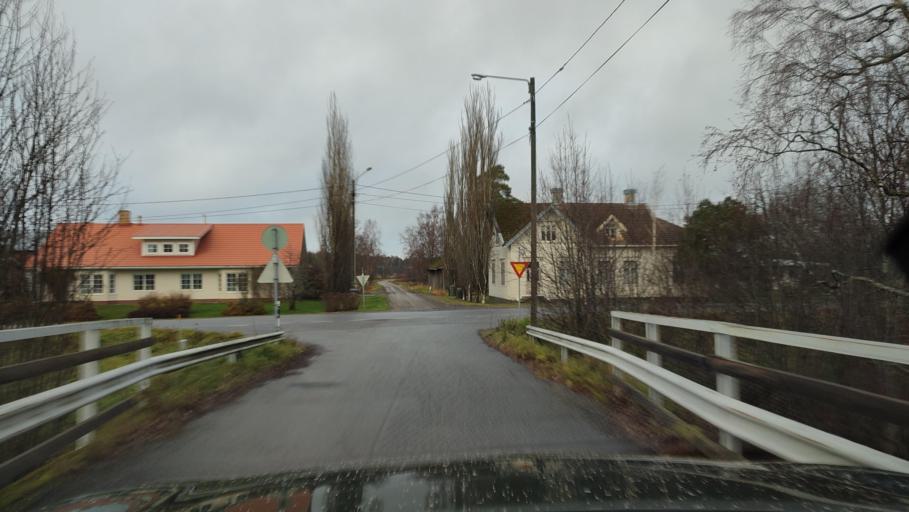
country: FI
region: Ostrobothnia
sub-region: Sydosterbotten
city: Kristinestad
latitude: 62.3026
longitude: 21.4538
